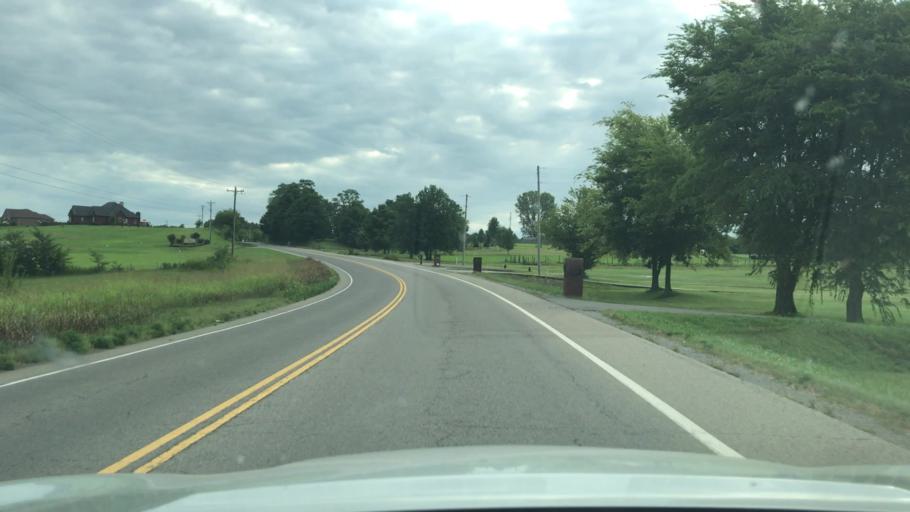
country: US
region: Kentucky
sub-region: Todd County
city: Guthrie
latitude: 36.6273
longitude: -87.2203
